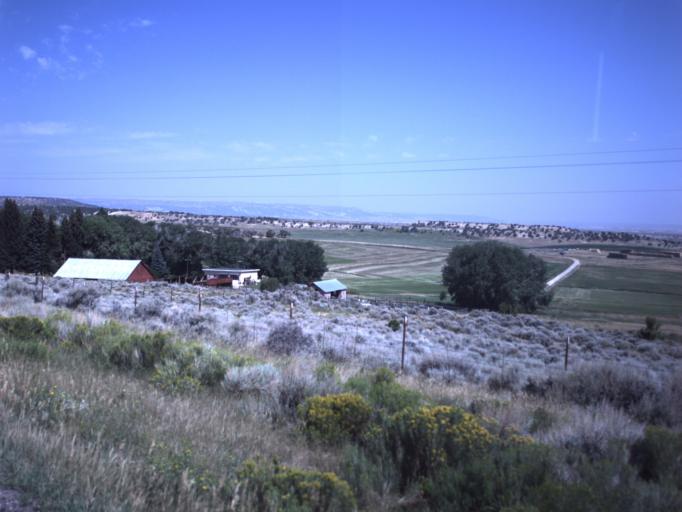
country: US
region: Utah
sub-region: Daggett County
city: Manila
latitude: 40.9774
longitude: -109.8319
